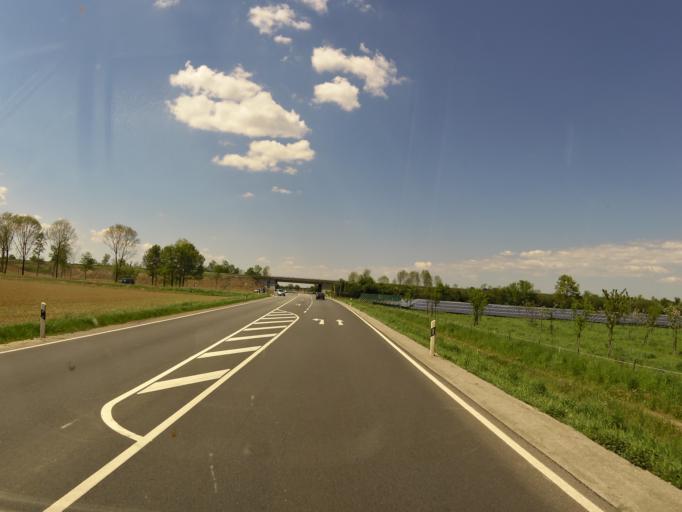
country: DE
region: Bavaria
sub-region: Lower Bavaria
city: Plattling
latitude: 48.7906
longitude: 12.8382
